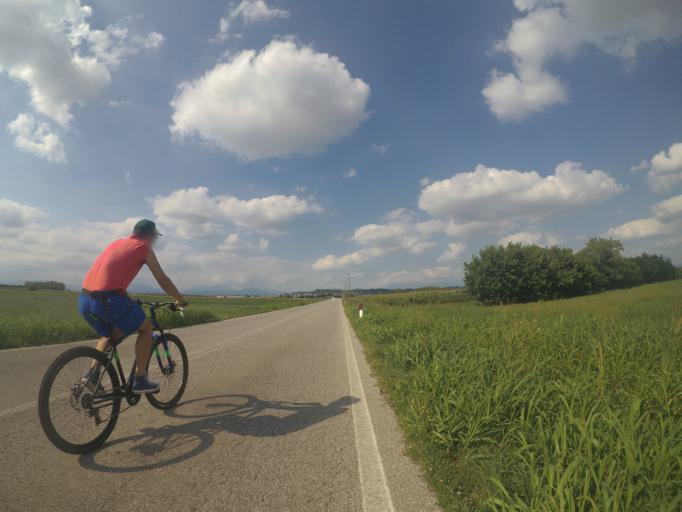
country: IT
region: Friuli Venezia Giulia
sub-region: Provincia di Udine
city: Fagagna
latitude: 46.0881
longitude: 13.0903
